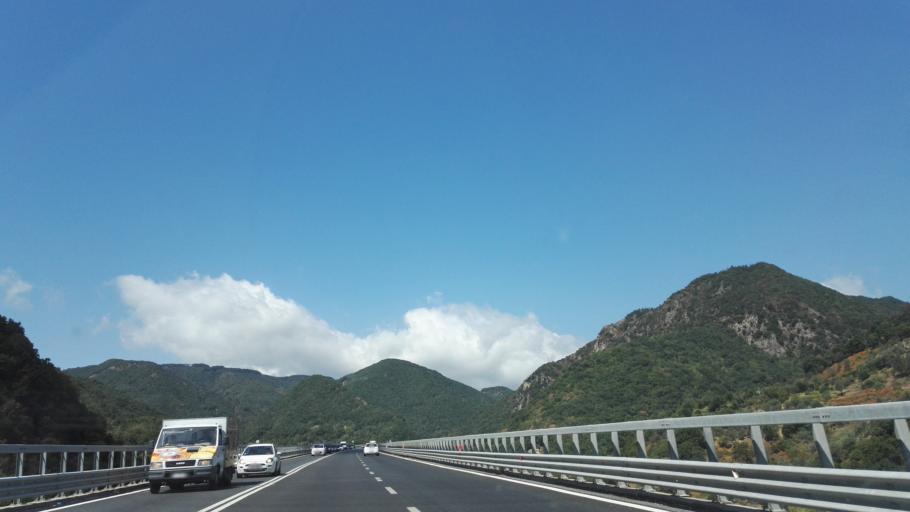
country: IT
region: Calabria
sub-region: Provincia di Reggio Calabria
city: Mammola
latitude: 38.3591
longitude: 16.2132
